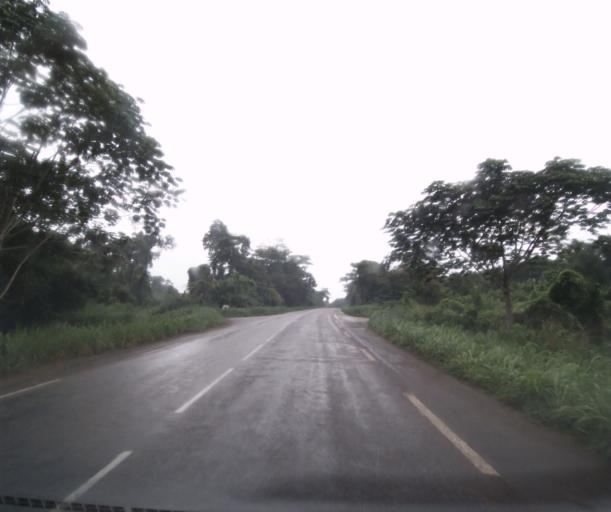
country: CM
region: Centre
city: Eseka
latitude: 3.8691
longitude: 10.6103
